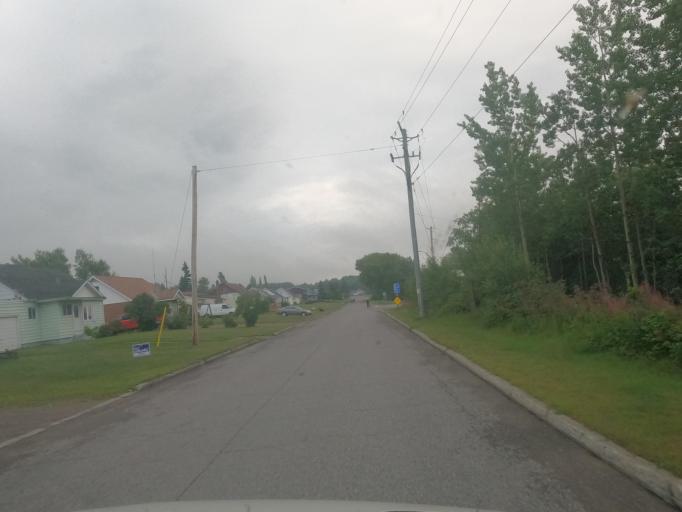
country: CA
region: Ontario
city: Marathon
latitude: 48.7807
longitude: -87.1034
